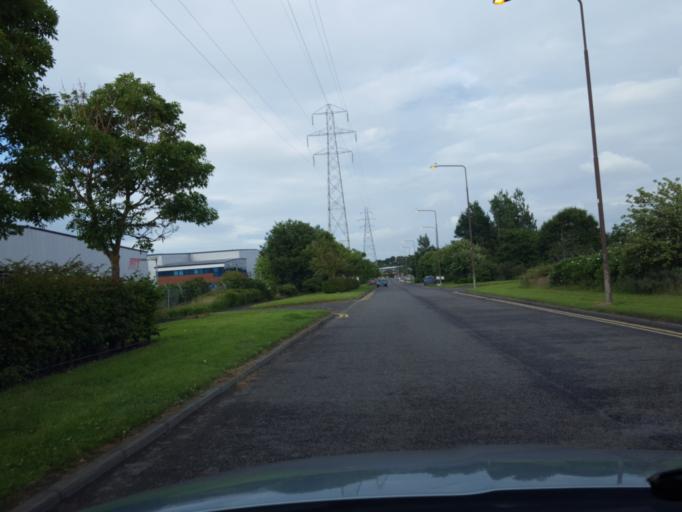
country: GB
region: Scotland
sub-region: West Lothian
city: Blackburn
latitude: 55.8846
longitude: -3.6319
